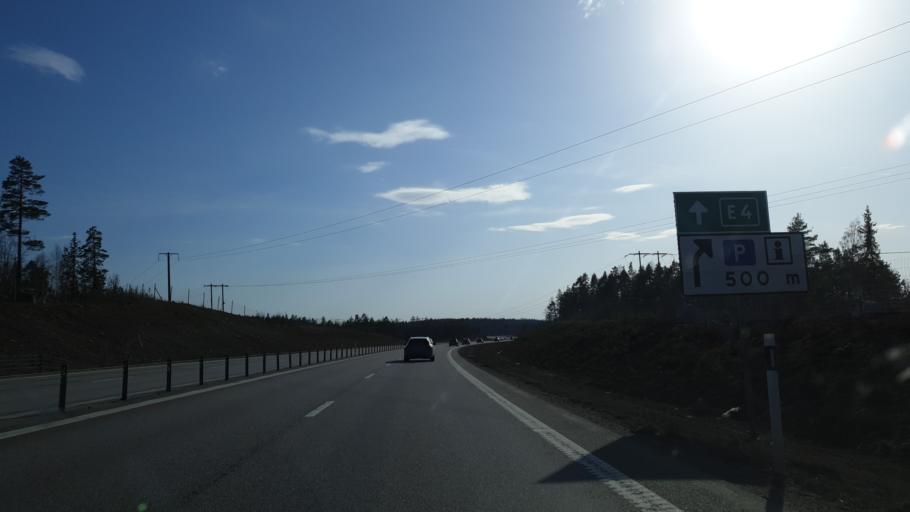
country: SE
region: Gaevleborg
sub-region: Hudiksvalls Kommun
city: Iggesund
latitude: 61.6877
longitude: 17.0513
